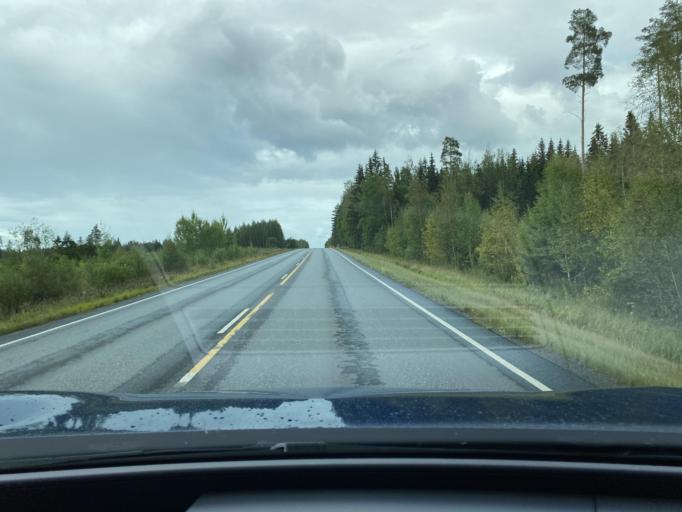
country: FI
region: Pirkanmaa
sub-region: Tampere
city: Haemeenkyroe
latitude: 61.6354
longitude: 23.1491
